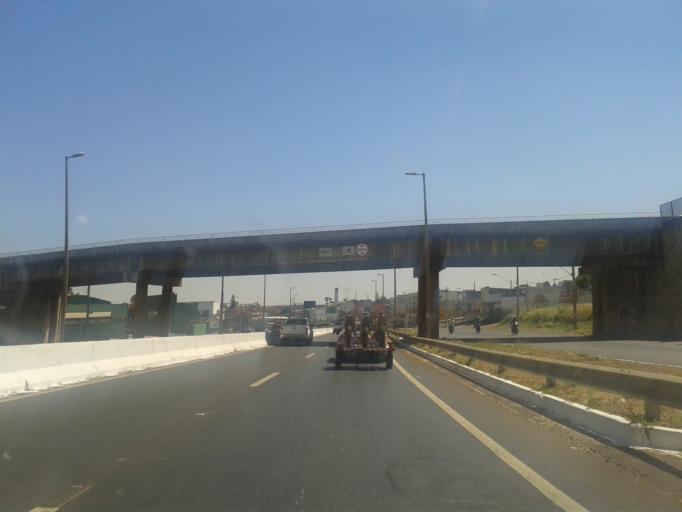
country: BR
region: Minas Gerais
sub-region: Uberlandia
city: Uberlandia
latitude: -18.9050
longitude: -48.2884
